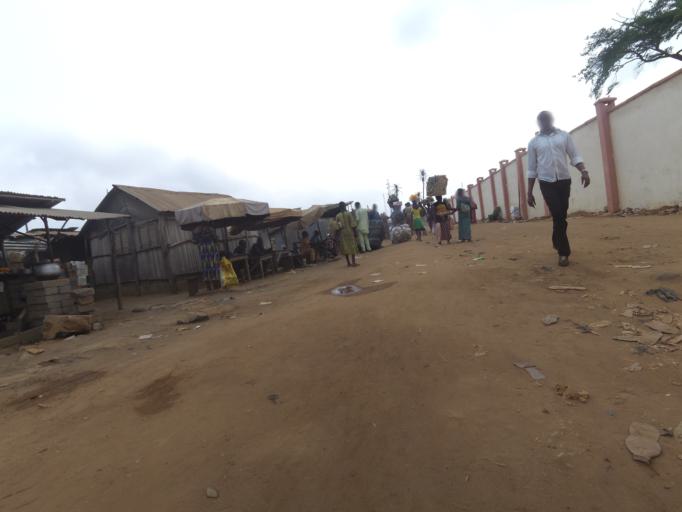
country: BJ
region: Queme
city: Porto-Novo
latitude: 6.3809
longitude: 2.7060
